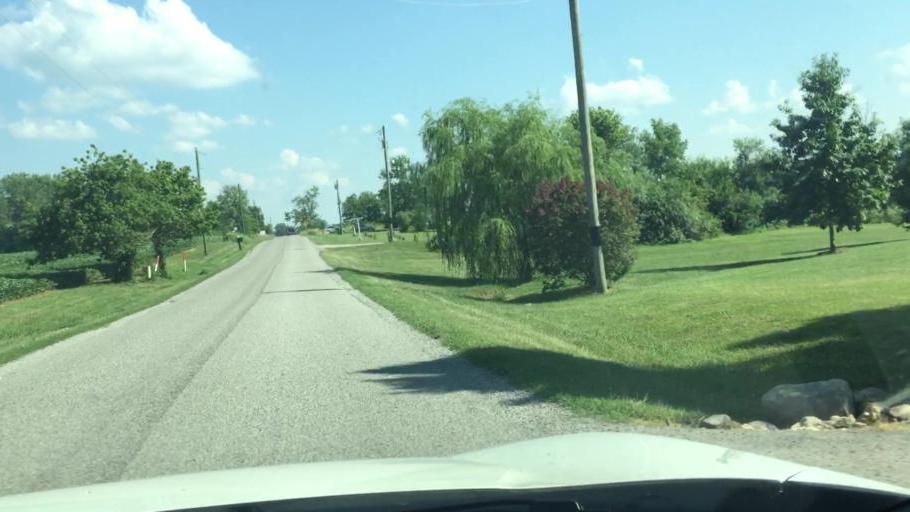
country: US
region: Ohio
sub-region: Champaign County
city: North Lewisburg
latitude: 40.2323
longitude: -83.5165
